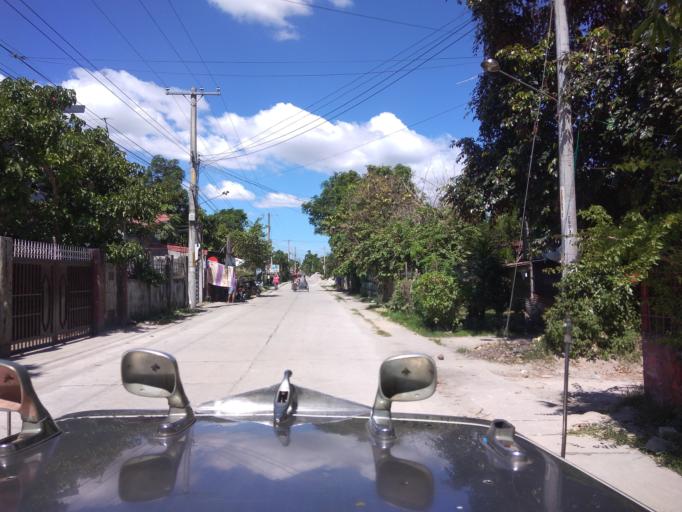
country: PH
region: Central Luzon
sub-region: Province of Pampanga
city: Magliman
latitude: 15.0388
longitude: 120.6458
